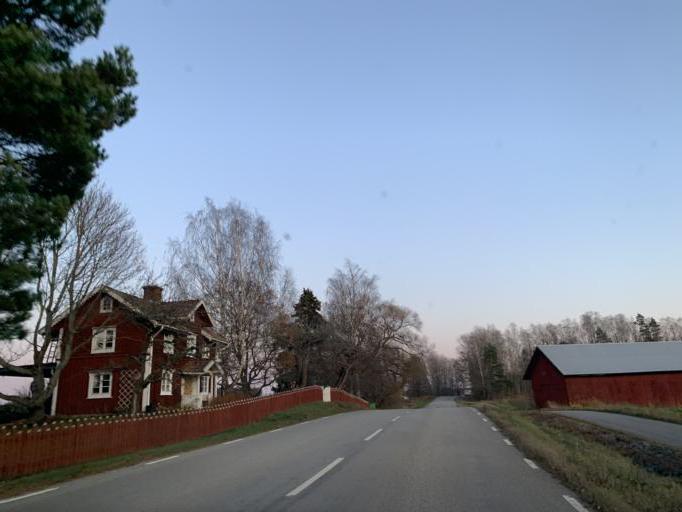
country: SE
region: OErebro
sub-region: Orebro Kommun
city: Hovsta
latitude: 59.3134
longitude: 15.3451
